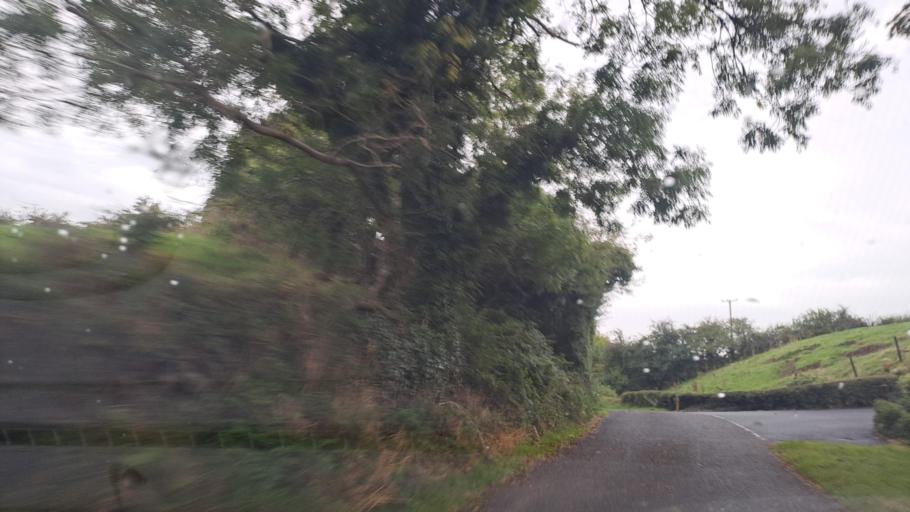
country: IE
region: Ulster
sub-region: County Monaghan
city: Carrickmacross
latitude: 53.9855
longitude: -6.7921
